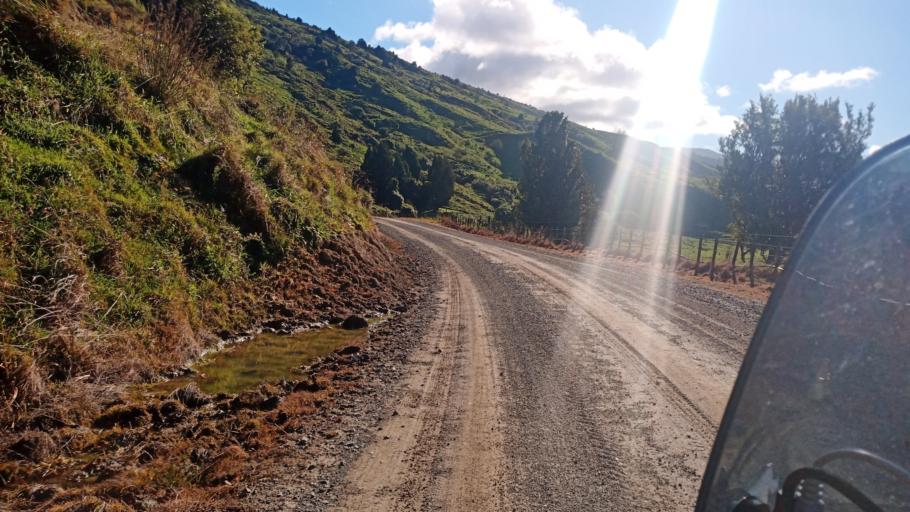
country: NZ
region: Hawke's Bay
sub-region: Wairoa District
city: Wairoa
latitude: -38.7498
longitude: 177.2693
